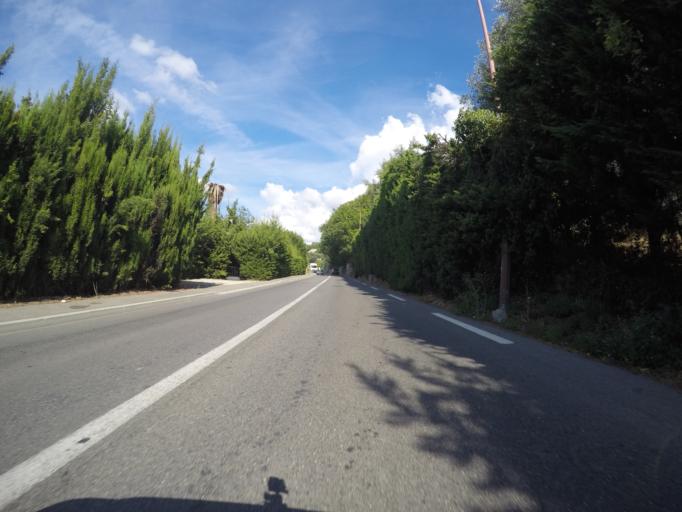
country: FR
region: Provence-Alpes-Cote d'Azur
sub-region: Departement des Alpes-Maritimes
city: Opio
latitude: 43.6763
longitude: 6.9836
